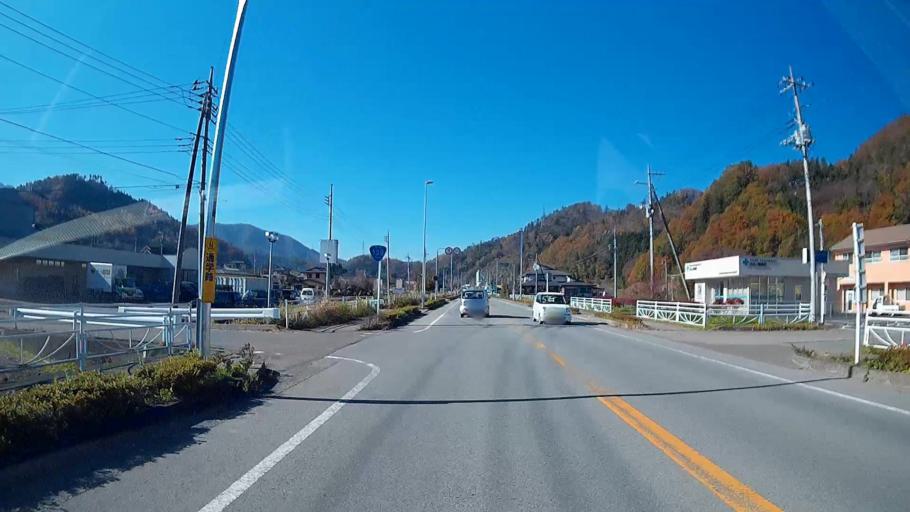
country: JP
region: Yamanashi
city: Otsuki
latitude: 35.5492
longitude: 138.9215
